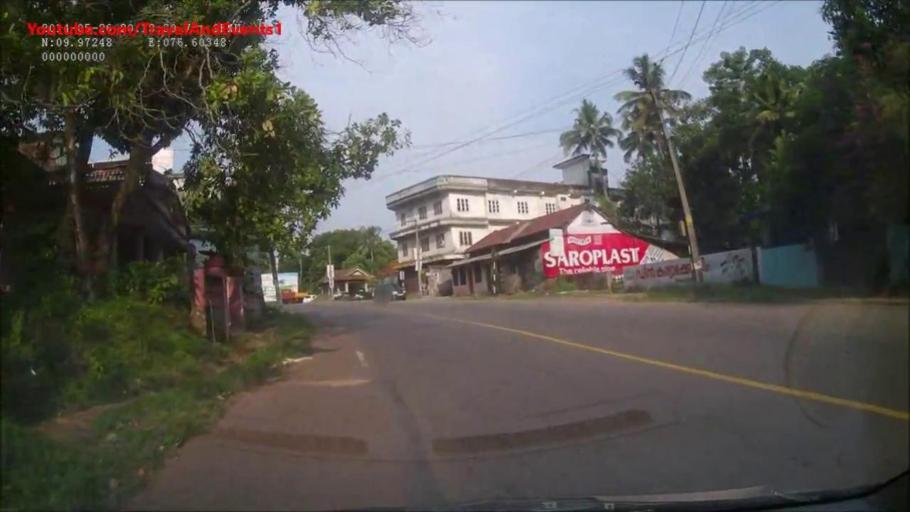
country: IN
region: Kerala
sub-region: Ernakulam
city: Muvattupula
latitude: 9.9658
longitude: 76.6136
